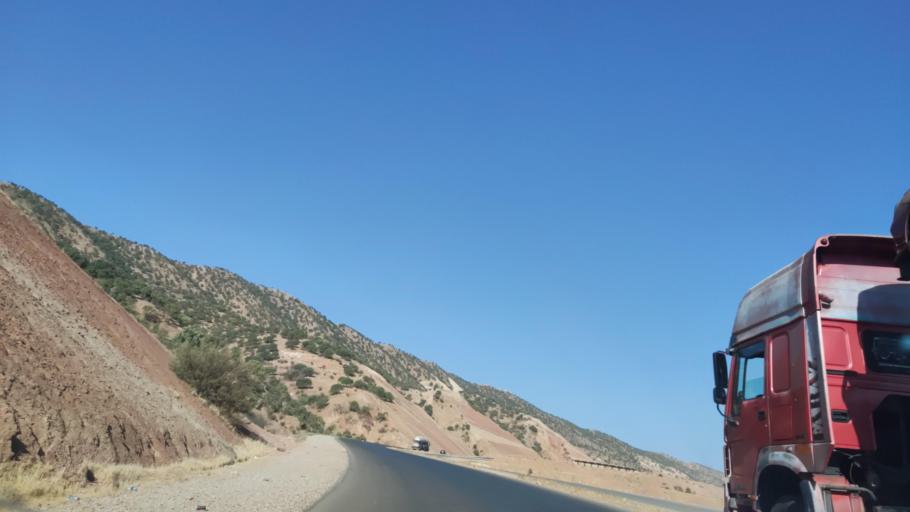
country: IQ
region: Arbil
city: Shaqlawah
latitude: 36.4328
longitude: 44.3098
